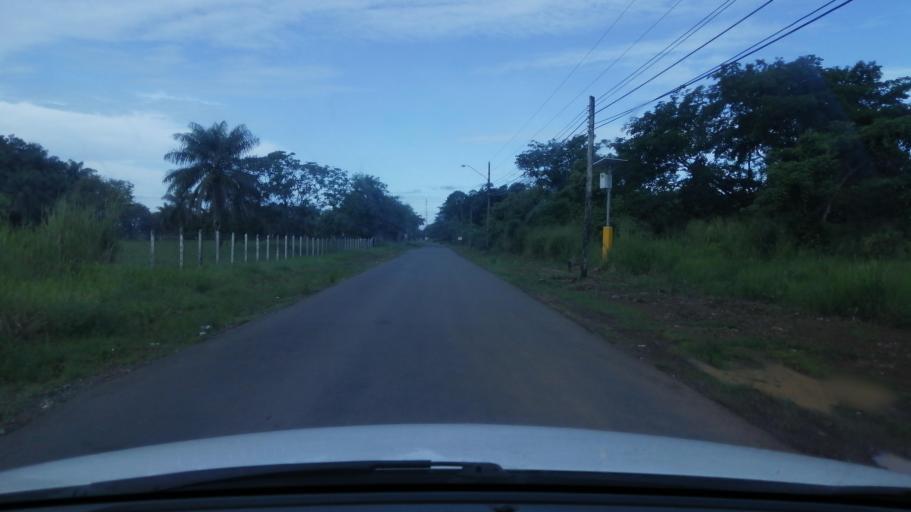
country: PA
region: Chiriqui
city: El Quiteno
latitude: 8.4651
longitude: -82.4151
